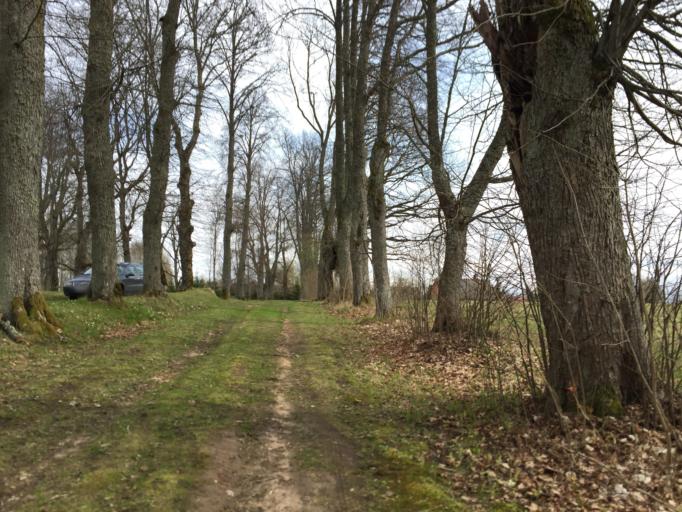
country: LV
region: Ligatne
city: Ligatne
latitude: 57.2175
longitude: 25.0680
